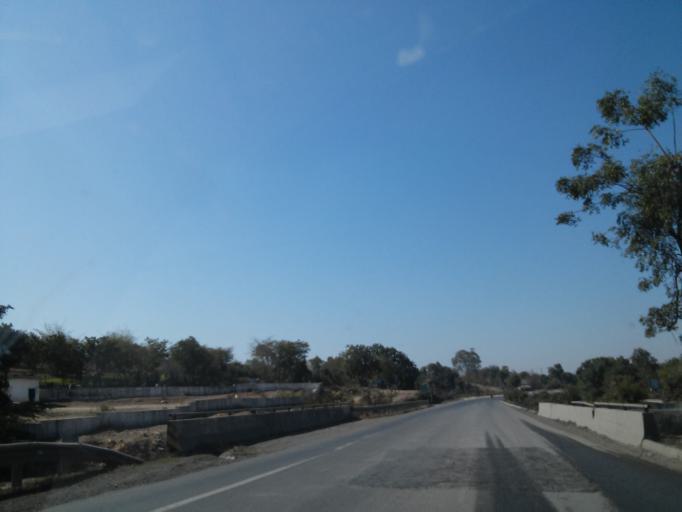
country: IN
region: Rajasthan
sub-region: Dungarpur
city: Dungarpur
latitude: 24.0032
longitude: 73.6532
